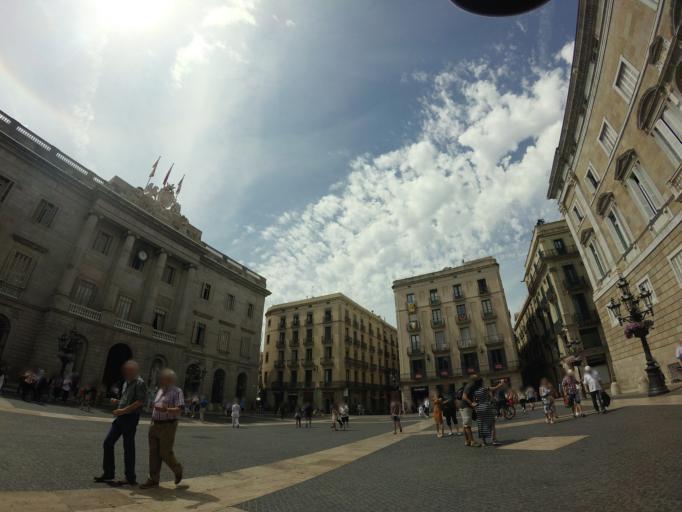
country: ES
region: Catalonia
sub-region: Provincia de Barcelona
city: Ciutat Vella
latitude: 41.3827
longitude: 2.1769
